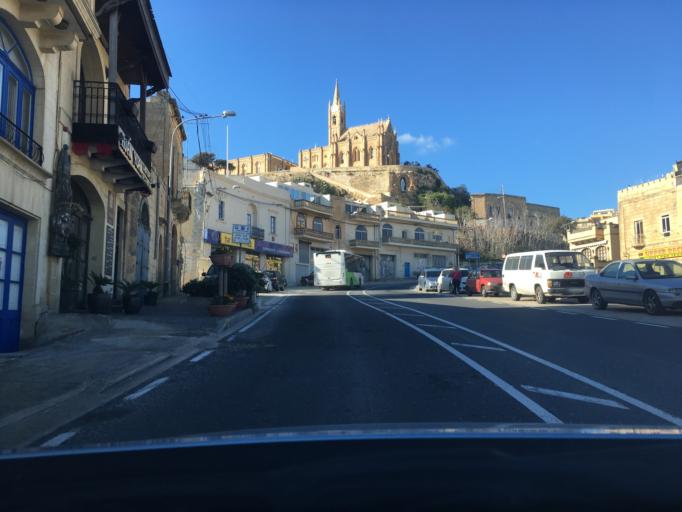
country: MT
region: Ghajnsielem
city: Mgarr
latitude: 36.0244
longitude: 14.2964
